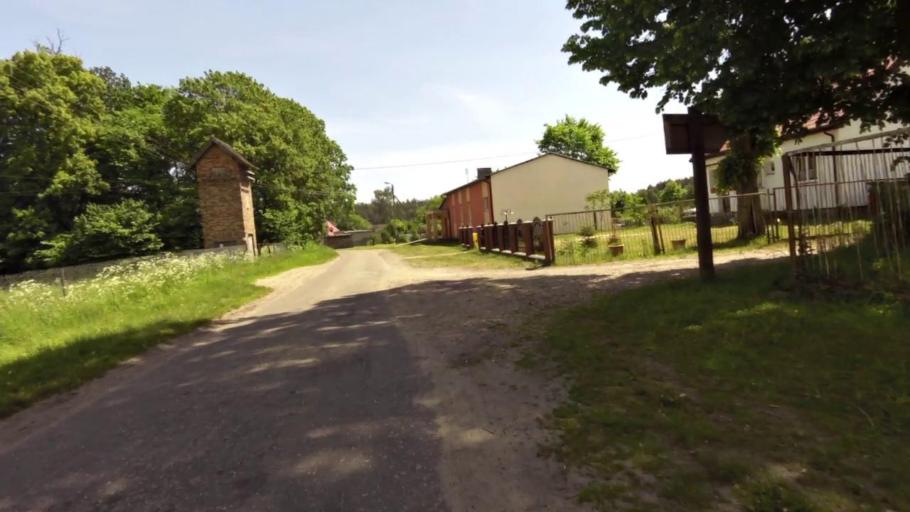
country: PL
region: West Pomeranian Voivodeship
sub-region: Powiat szczecinecki
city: Szczecinek
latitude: 53.6296
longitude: 16.6821
